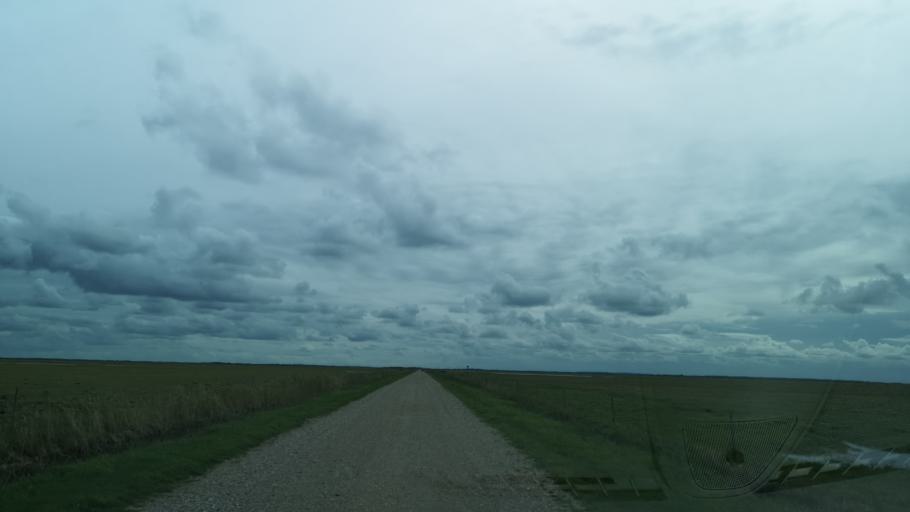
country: DK
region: Central Jutland
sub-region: Ringkobing-Skjern Kommune
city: Hvide Sande
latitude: 55.8911
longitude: 8.2161
